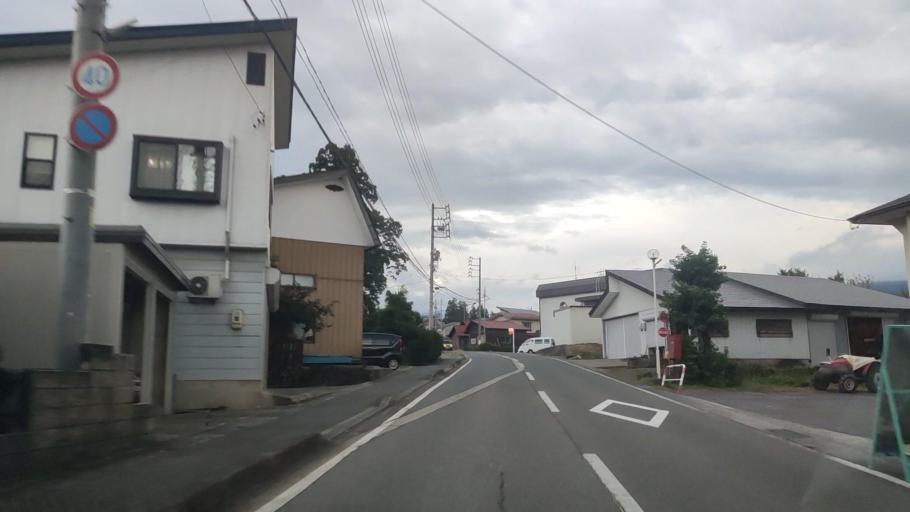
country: JP
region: Nagano
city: Iiyama
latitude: 36.8579
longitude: 138.4079
